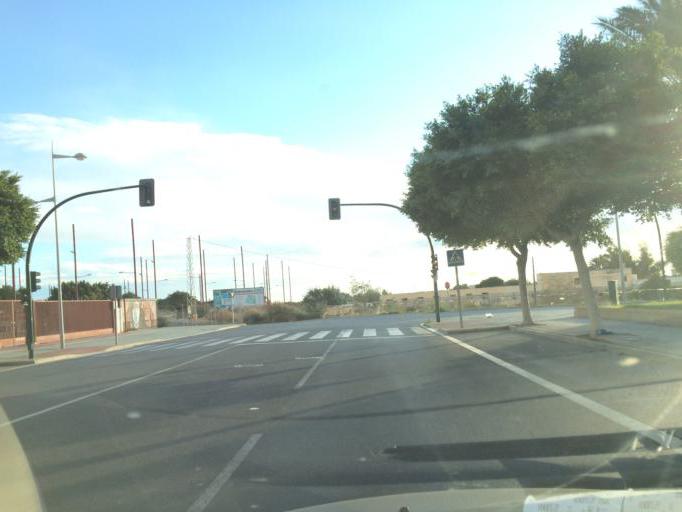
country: ES
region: Andalusia
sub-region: Provincia de Almeria
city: Almeria
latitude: 36.8348
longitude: -2.4322
